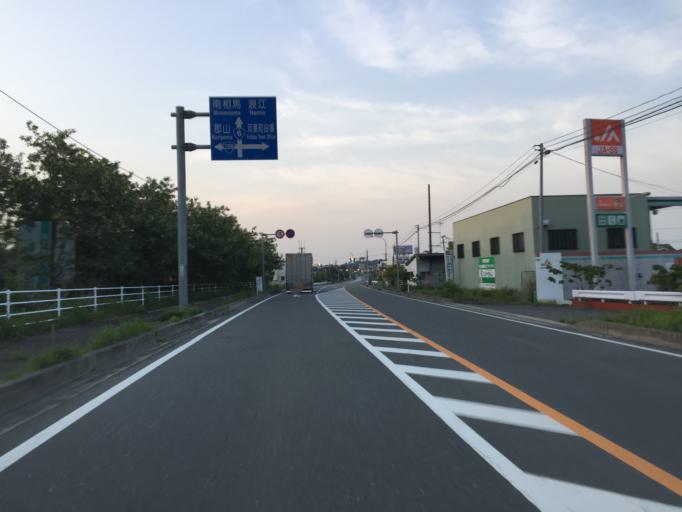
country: JP
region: Fukushima
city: Namie
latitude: 37.4460
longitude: 141.0085
